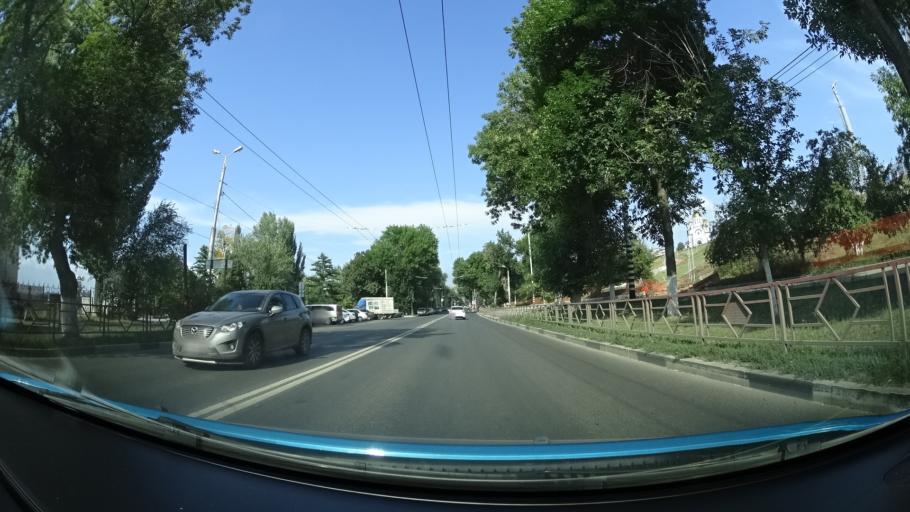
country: RU
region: Samara
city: Samara
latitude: 53.2045
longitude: 50.1070
